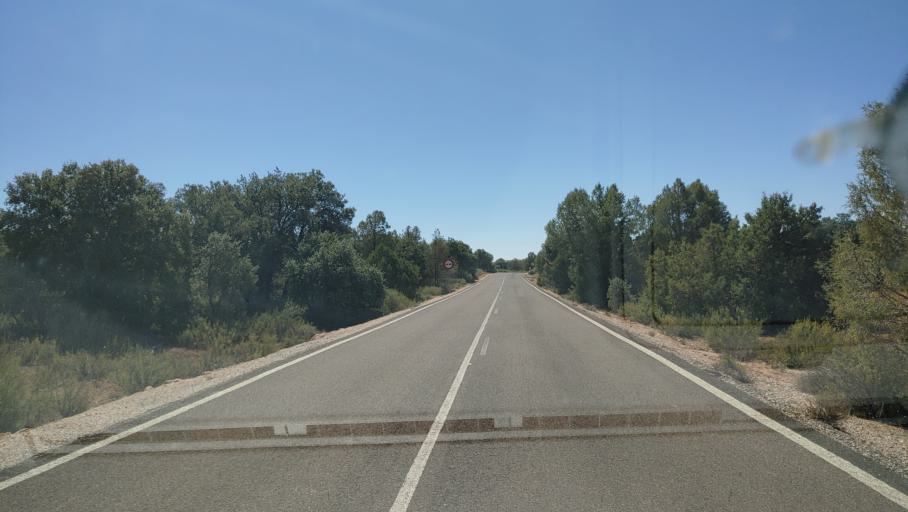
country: ES
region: Castille-La Mancha
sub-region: Provincia de Albacete
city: Ossa de Montiel
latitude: 38.8816
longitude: -2.7773
